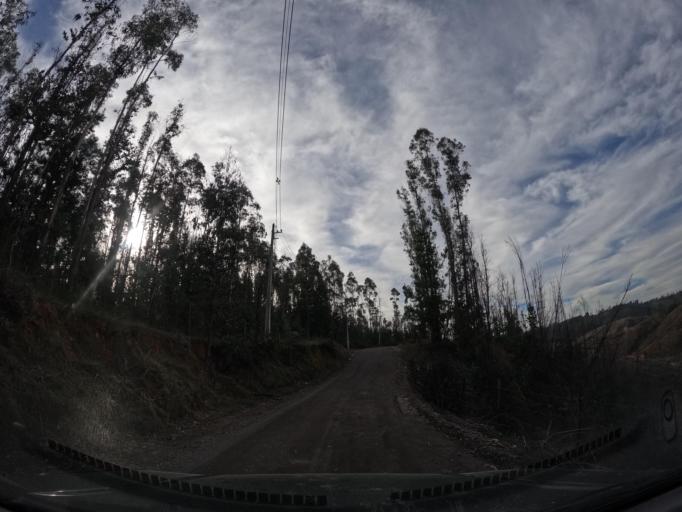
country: CL
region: Biobio
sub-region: Provincia de Concepcion
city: Chiguayante
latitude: -37.0214
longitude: -72.9100
